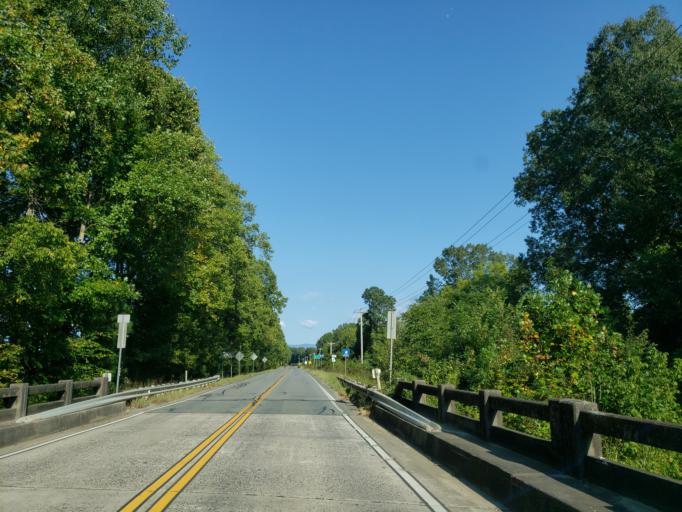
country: US
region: Georgia
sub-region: Whitfield County
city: Varnell
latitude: 34.9213
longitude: -84.8414
